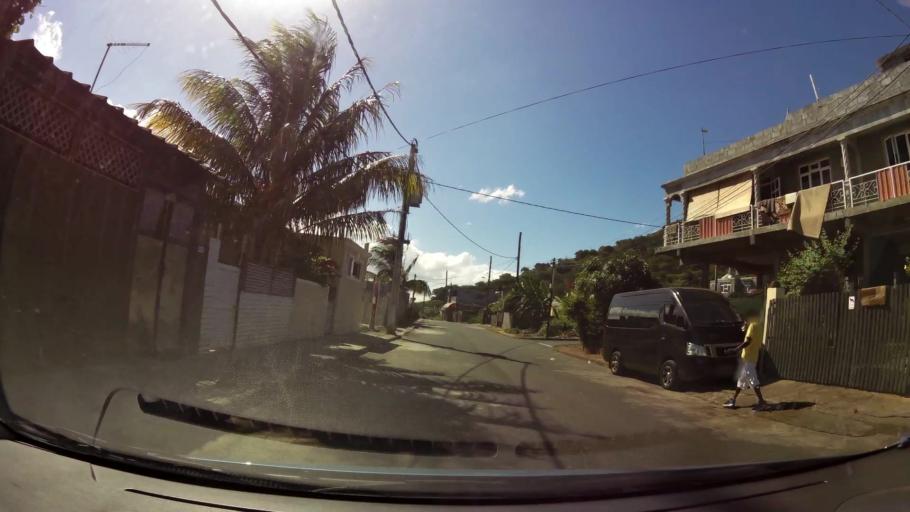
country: MU
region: Black River
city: Cascavelle
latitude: -20.2667
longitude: 57.4208
